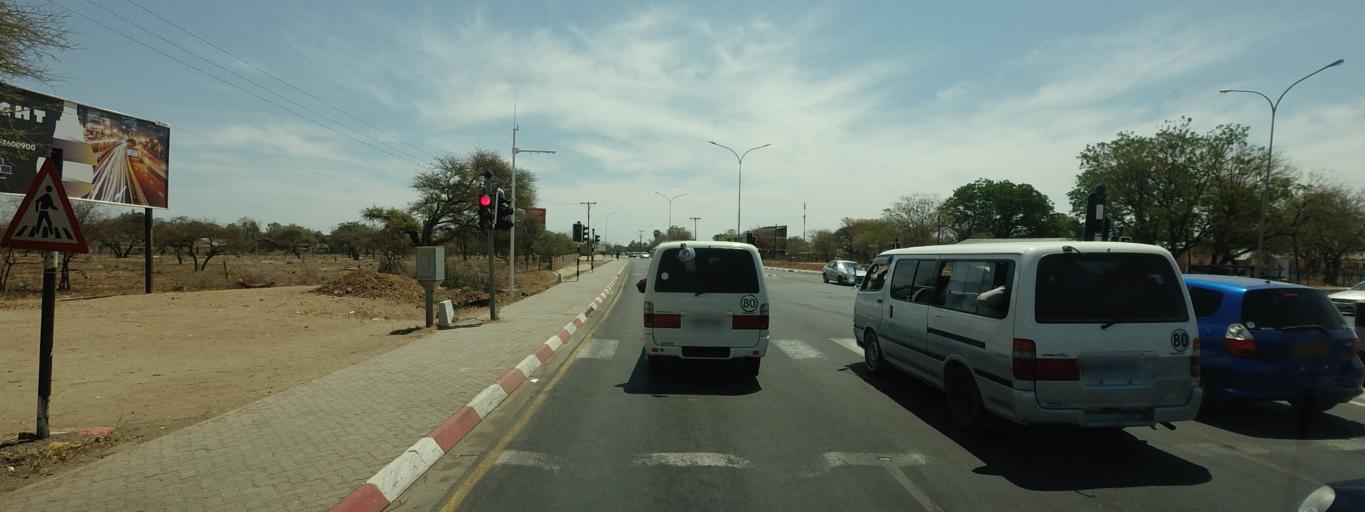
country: BW
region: North East
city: Francistown
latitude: -21.1721
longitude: 27.5063
